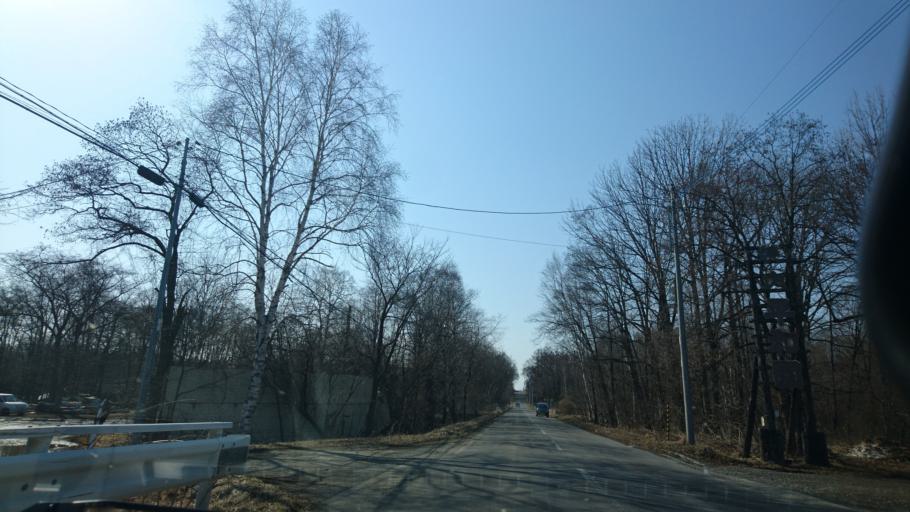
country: JP
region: Hokkaido
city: Obihiro
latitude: 42.9143
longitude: 143.1040
